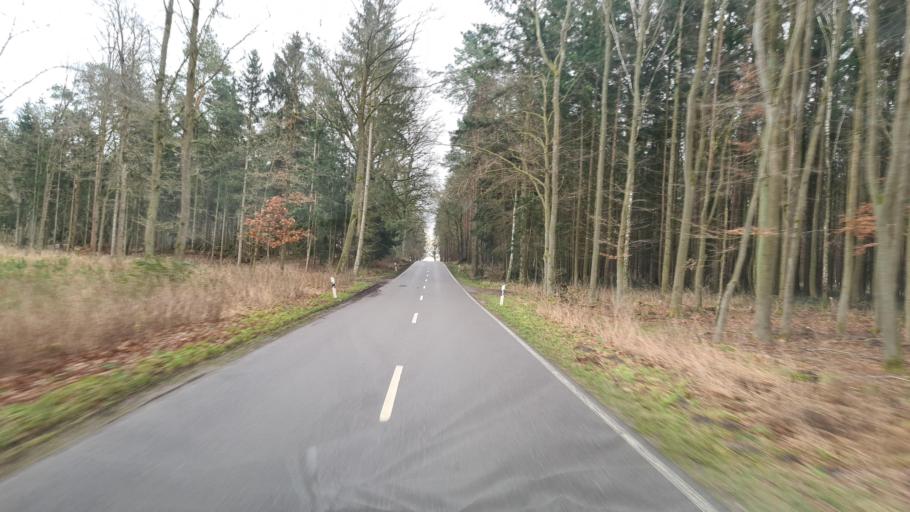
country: DE
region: Brandenburg
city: Zehdenick
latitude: 52.9361
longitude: 13.2358
